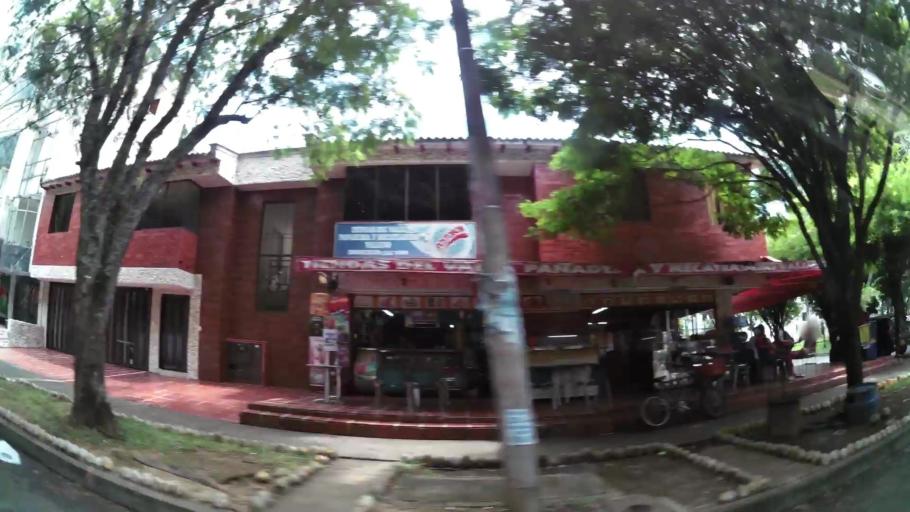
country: CO
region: Valle del Cauca
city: Cali
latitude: 3.3831
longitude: -76.5302
